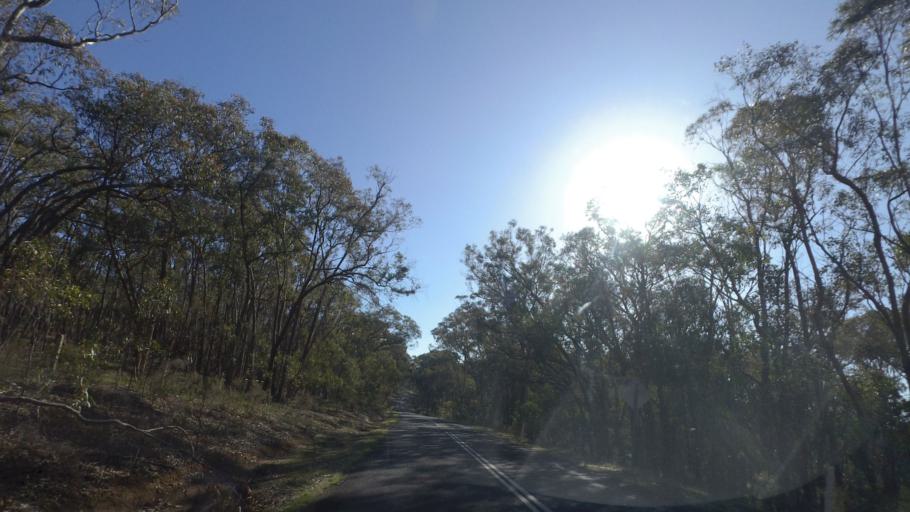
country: AU
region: Victoria
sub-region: Greater Bendigo
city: Kangaroo Flat
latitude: -36.8851
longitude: 144.2855
